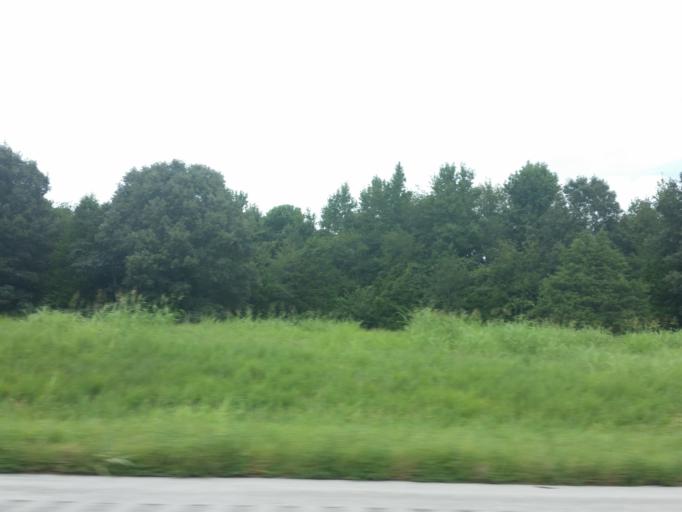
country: US
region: Kentucky
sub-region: Trigg County
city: Cadiz
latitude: 36.9419
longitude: -87.8333
